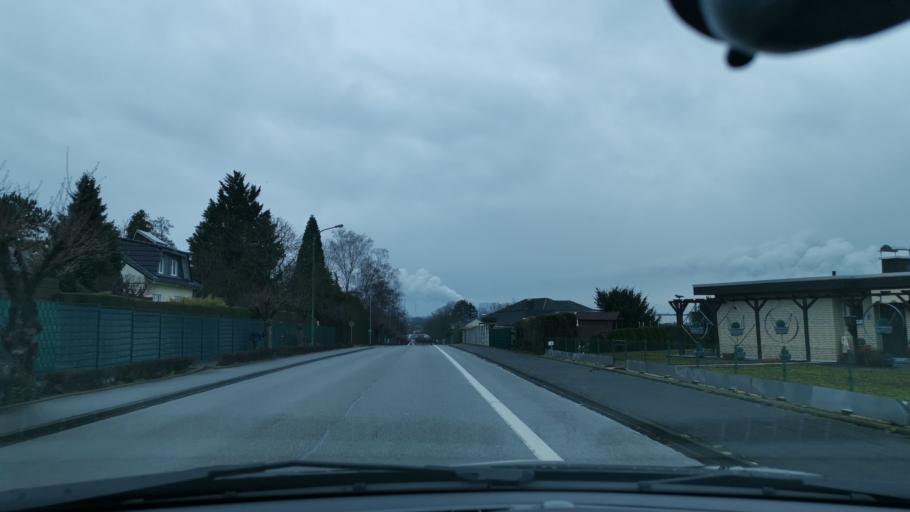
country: DE
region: North Rhine-Westphalia
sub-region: Regierungsbezirk Koln
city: Bedburg
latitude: 51.0030
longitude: 6.5449
